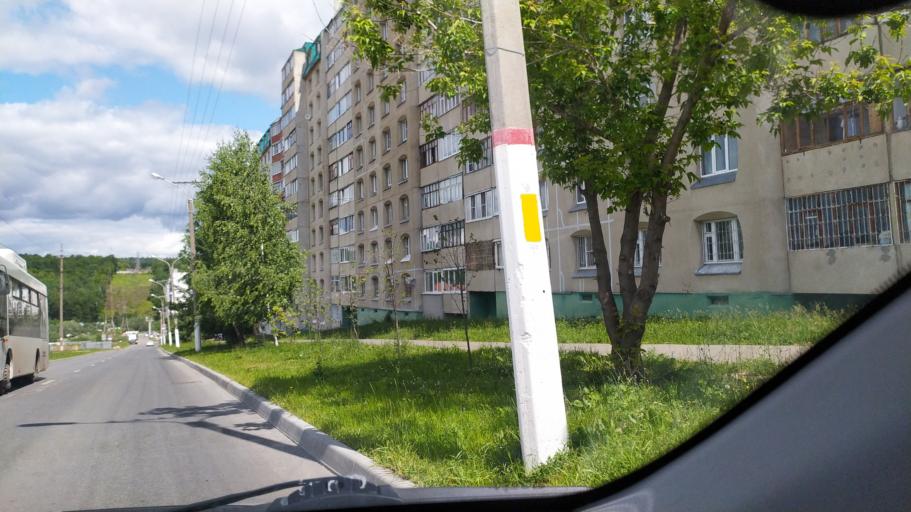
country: RU
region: Chuvashia
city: Novyye Lapsary
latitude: 56.1191
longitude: 47.1751
